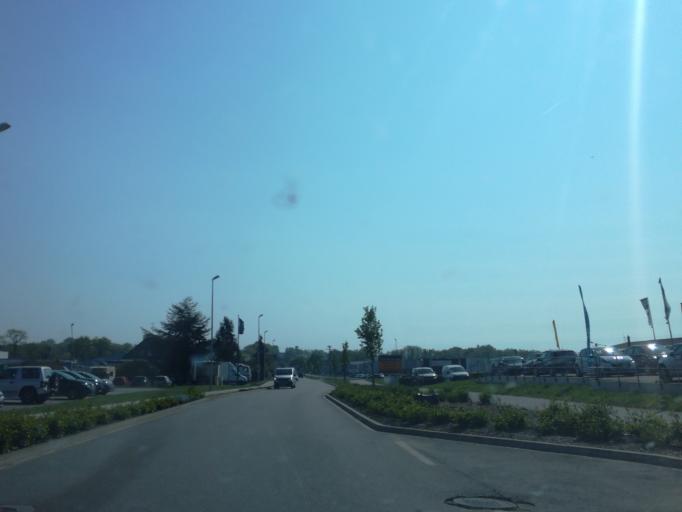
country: FR
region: Brittany
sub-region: Departement du Morbihan
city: Saint-Thuriau
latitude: 48.0389
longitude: -2.9618
